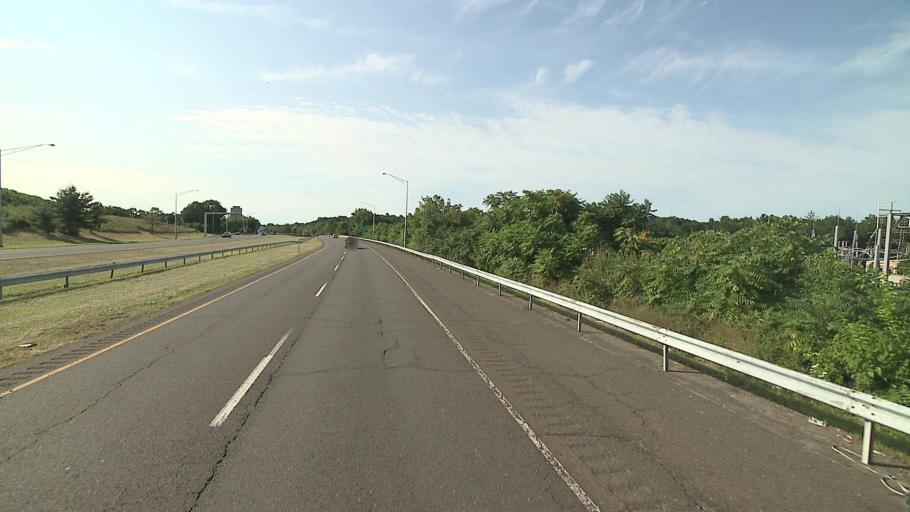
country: US
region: Connecticut
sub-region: Fairfield County
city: Norwalk
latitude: 41.1285
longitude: -73.4278
